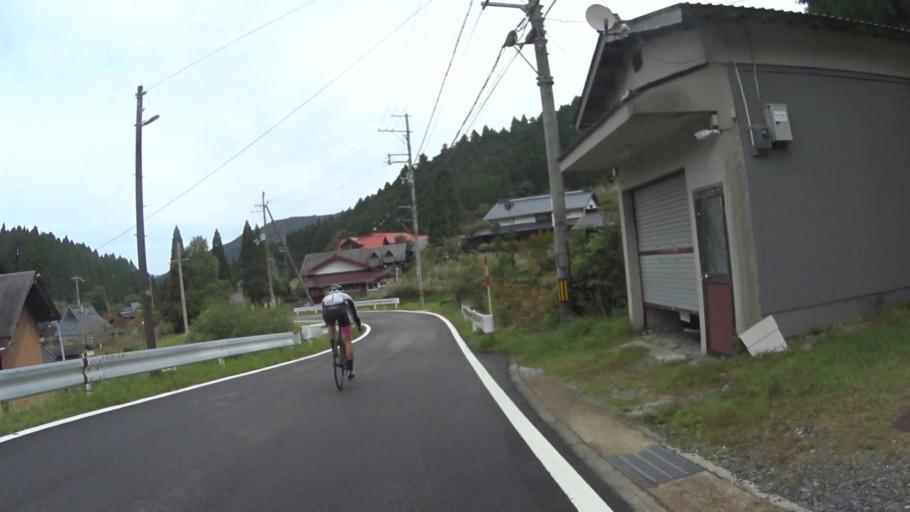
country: JP
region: Shiga Prefecture
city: Kitahama
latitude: 35.1644
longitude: 135.7802
